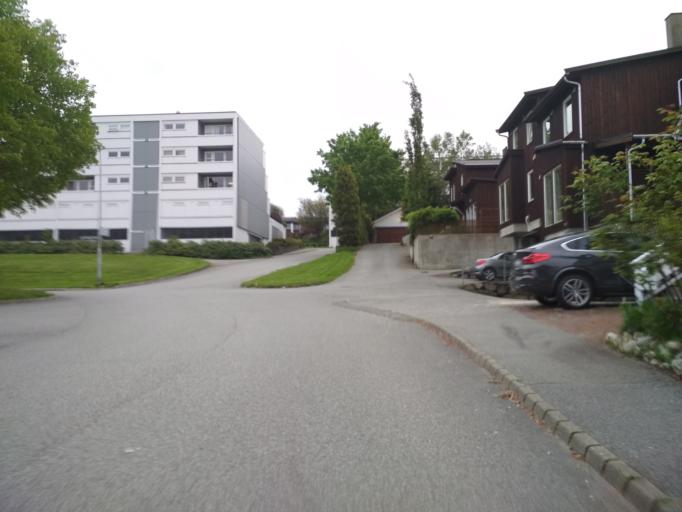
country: NO
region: Rogaland
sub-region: Stavanger
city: Stavanger
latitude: 58.9534
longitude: 5.6970
